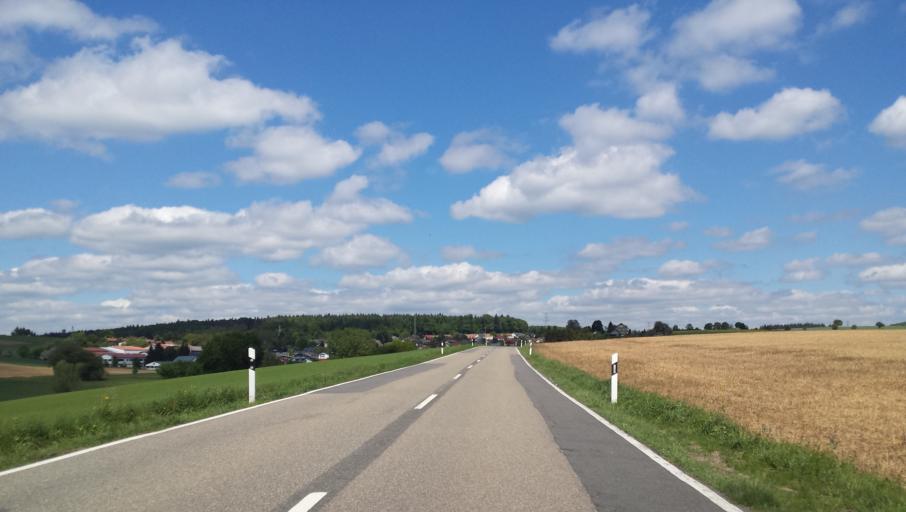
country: DE
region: Baden-Wuerttemberg
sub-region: Karlsruhe Region
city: Neunkirchen
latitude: 49.3951
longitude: 8.9716
